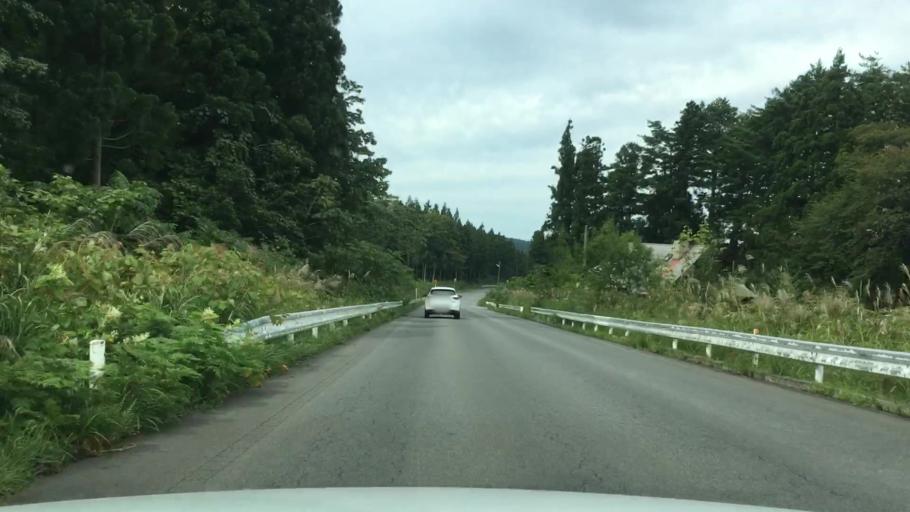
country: JP
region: Aomori
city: Shimokizukuri
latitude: 40.7100
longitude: 140.2752
